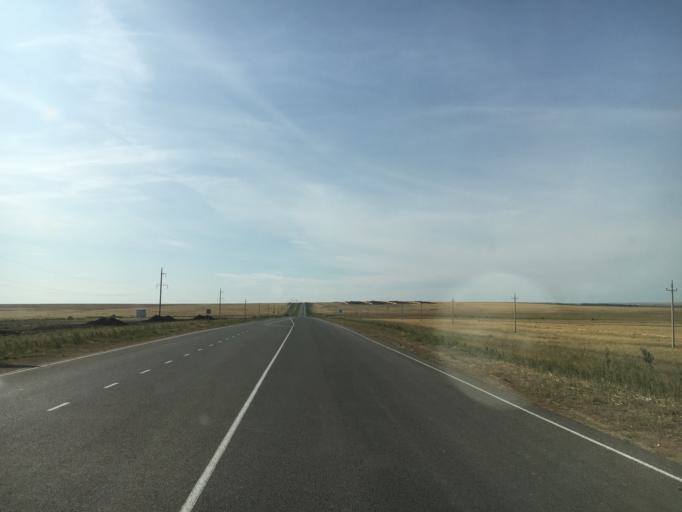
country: KZ
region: Batys Qazaqstan
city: Kamenka
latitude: 51.1201
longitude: 50.1889
